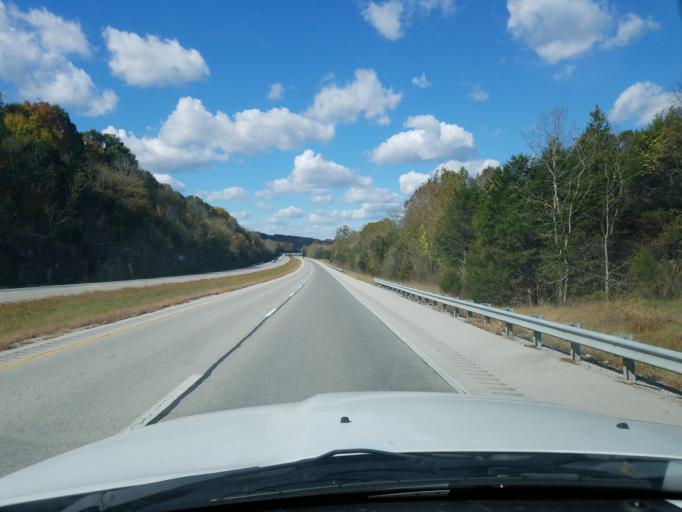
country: US
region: Kentucky
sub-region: Warren County
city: Bowling Green
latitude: 37.0400
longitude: -86.5629
